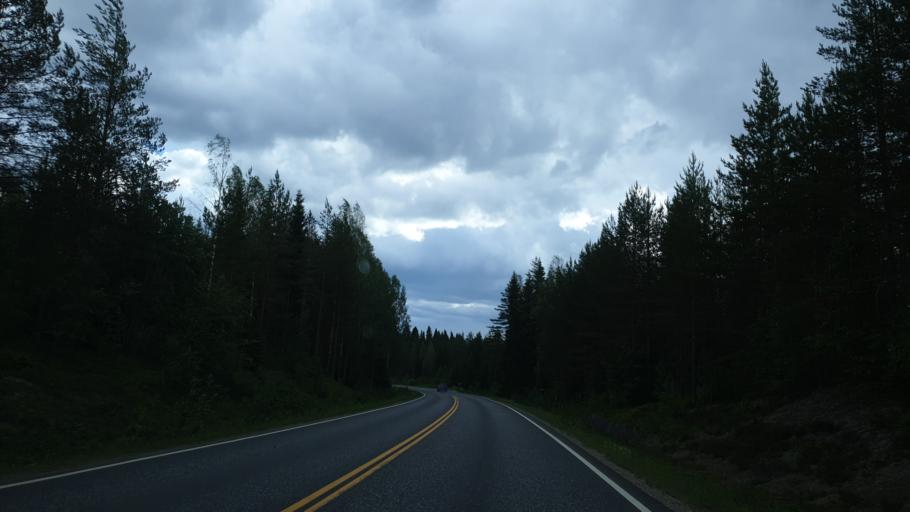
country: FI
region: Northern Savo
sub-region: Koillis-Savo
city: Kaavi
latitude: 62.9560
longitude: 28.4024
